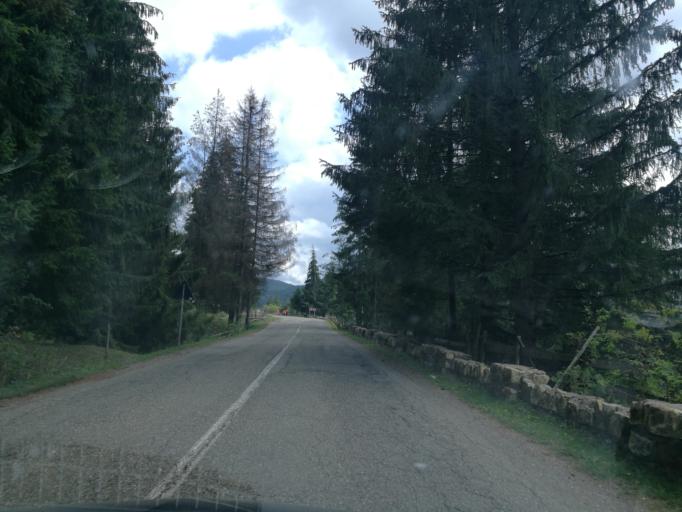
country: RO
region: Suceava
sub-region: Comuna Vatra Moldovitei
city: Vatra Moldovitei
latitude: 47.7267
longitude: 25.6115
